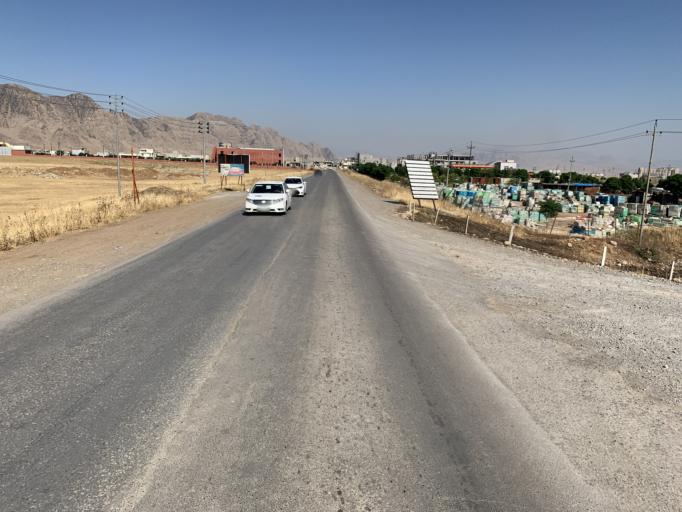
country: IQ
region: As Sulaymaniyah
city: Raniye
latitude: 36.2622
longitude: 44.8521
